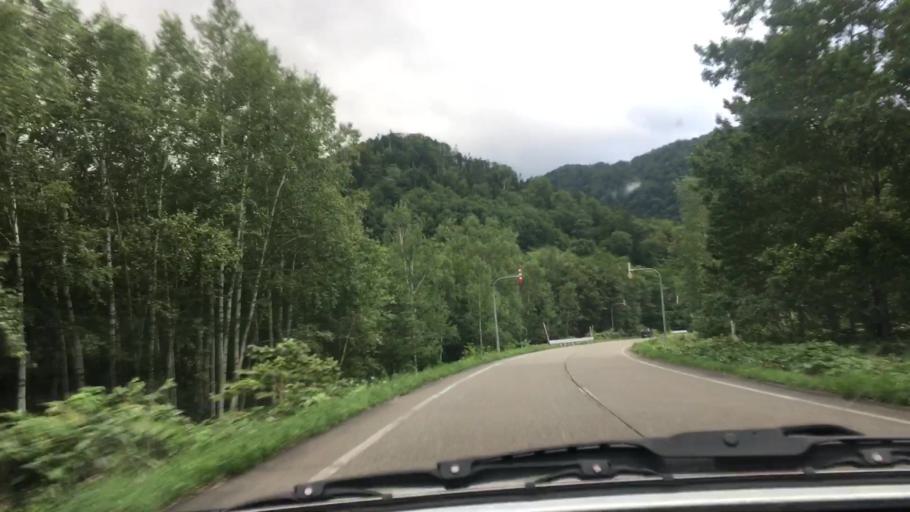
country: JP
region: Hokkaido
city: Shimo-furano
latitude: 43.0453
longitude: 142.5320
